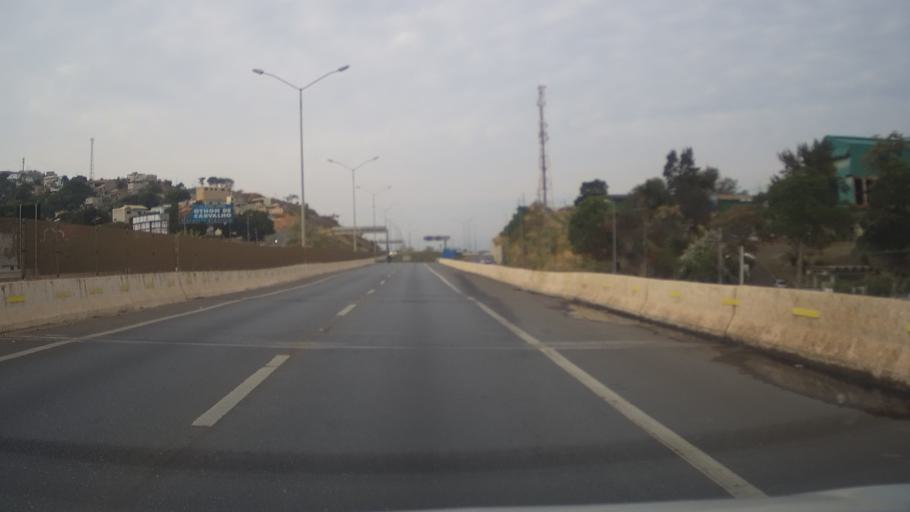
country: BR
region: Minas Gerais
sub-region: Vespasiano
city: Vespasiano
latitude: -19.7564
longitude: -43.9478
